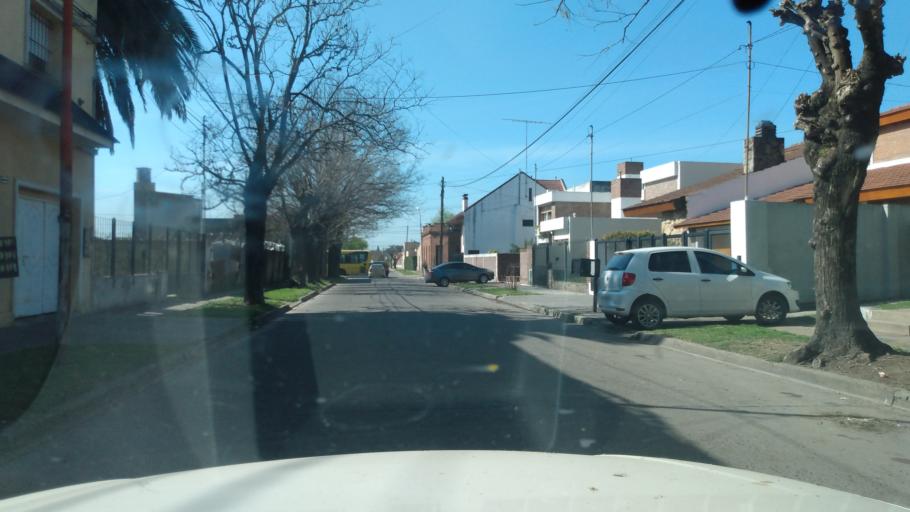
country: AR
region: Buenos Aires
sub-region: Partido de Lujan
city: Lujan
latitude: -34.5710
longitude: -59.1001
